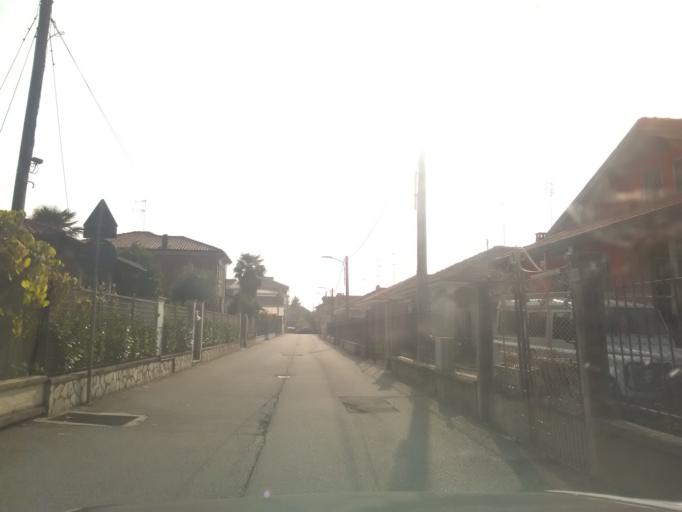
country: IT
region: Piedmont
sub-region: Provincia di Vercelli
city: Santhia
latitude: 45.3694
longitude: 8.1660
